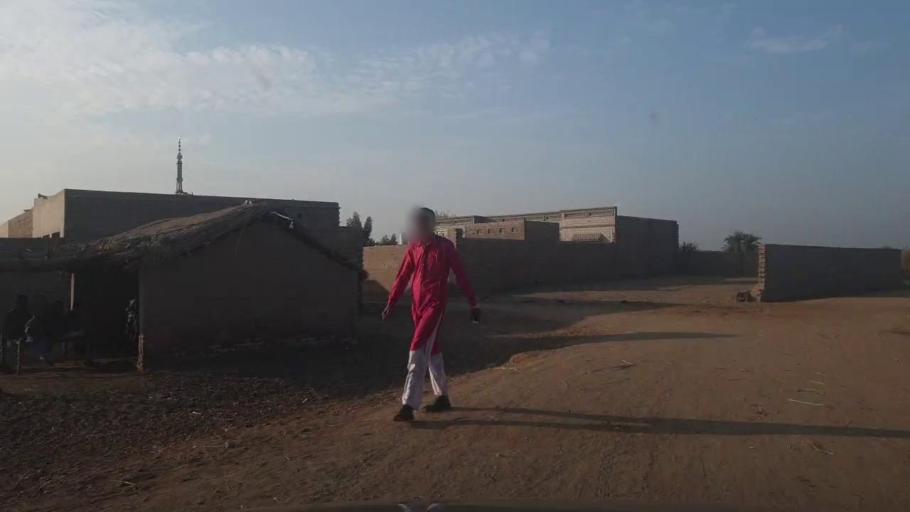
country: PK
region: Sindh
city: Sakrand
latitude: 26.0747
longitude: 68.4017
